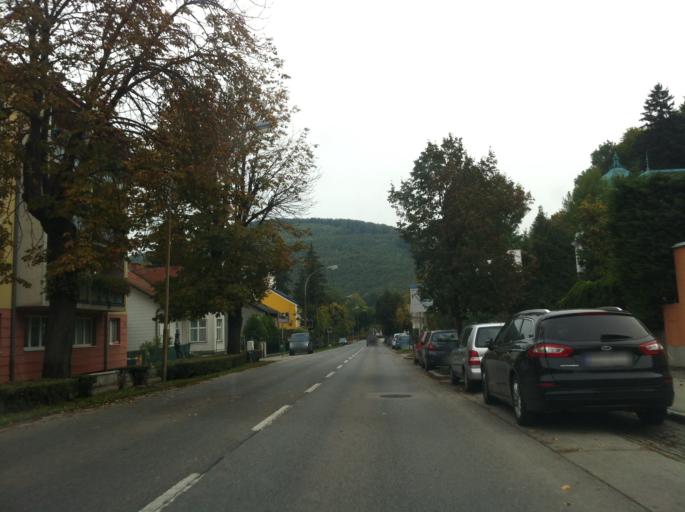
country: AT
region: Lower Austria
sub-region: Politischer Bezirk Wien-Umgebung
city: Purkersdorf
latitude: 48.2128
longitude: 16.1721
